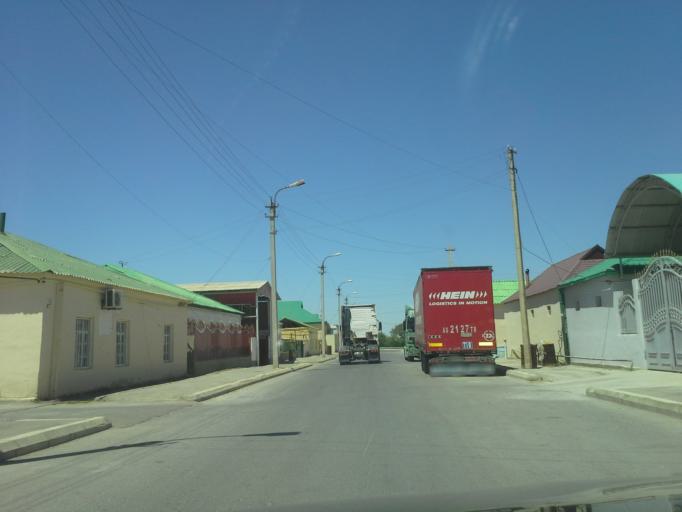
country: TM
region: Ahal
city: Abadan
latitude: 38.0332
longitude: 58.2626
